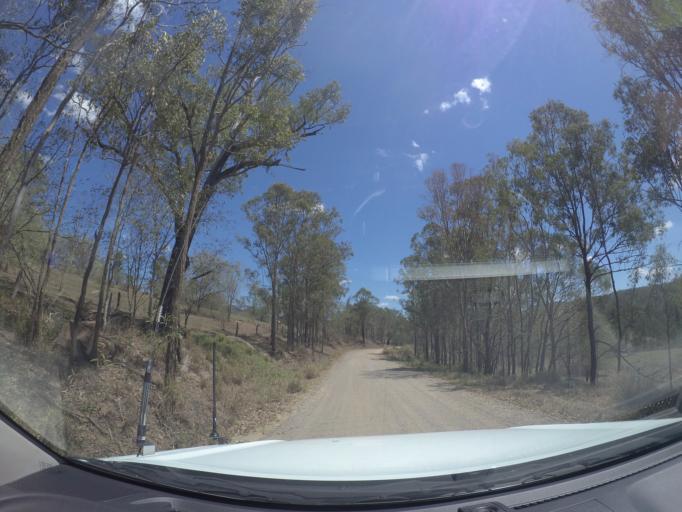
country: AU
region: Queensland
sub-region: Logan
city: North Maclean
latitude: -27.8346
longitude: 152.8693
